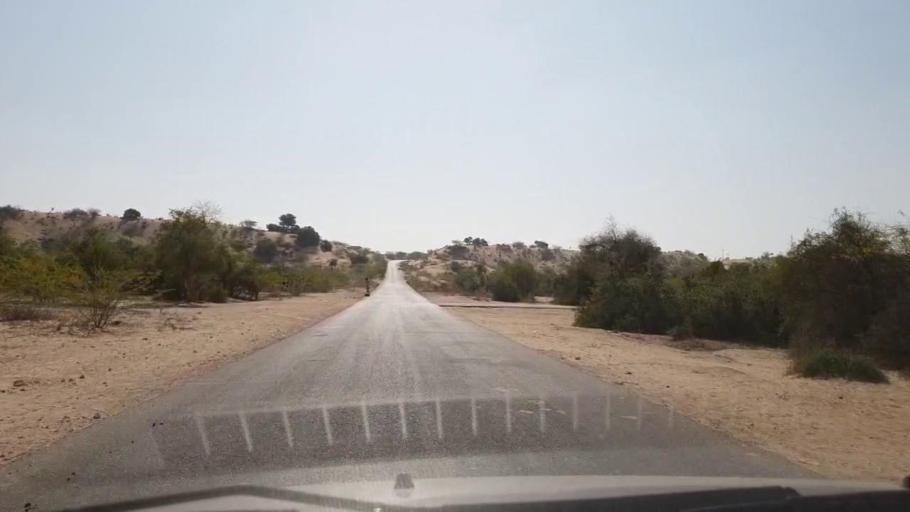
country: PK
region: Sindh
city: Mithi
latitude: 24.5938
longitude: 69.7130
